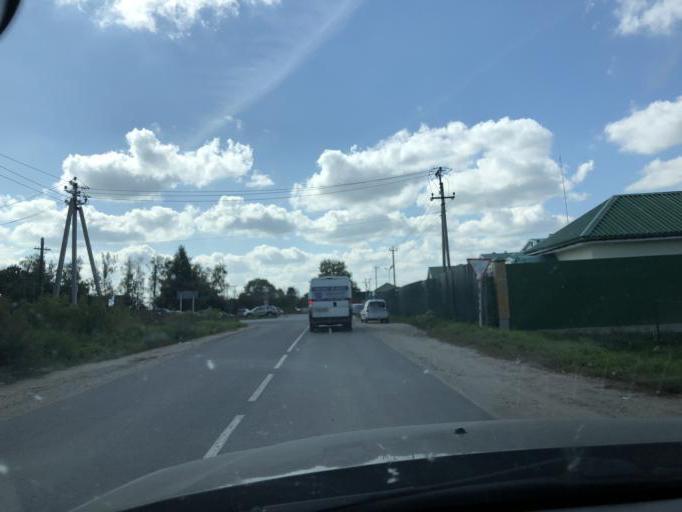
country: RU
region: Tula
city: Yasnogorsk
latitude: 54.4893
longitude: 37.6889
